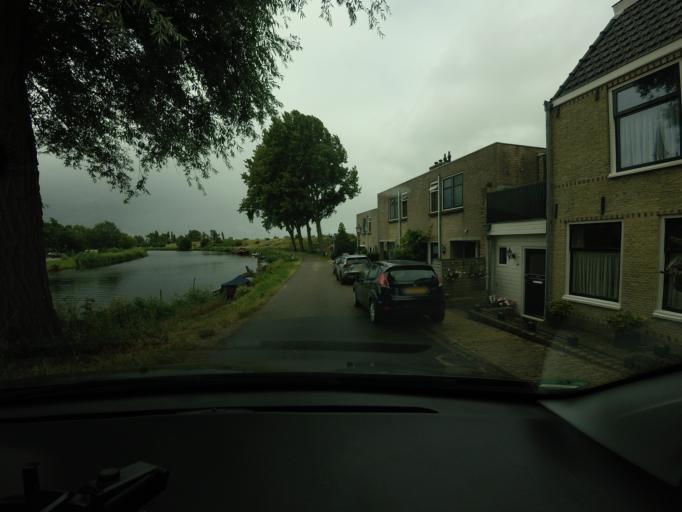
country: NL
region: North Holland
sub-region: Gemeente Velsen
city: Velsen-Zuid
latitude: 52.4151
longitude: 4.6769
